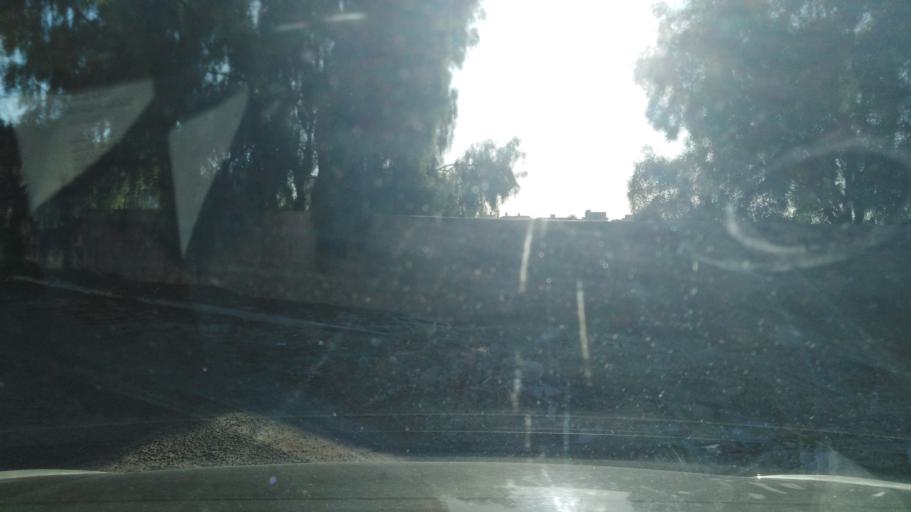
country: TN
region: Qabis
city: Gabes
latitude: 33.9551
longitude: 10.0086
